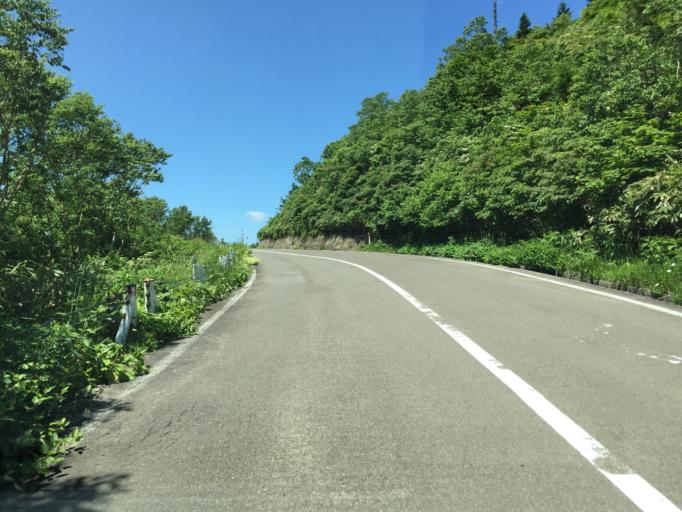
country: JP
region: Fukushima
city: Inawashiro
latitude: 37.6920
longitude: 140.2465
